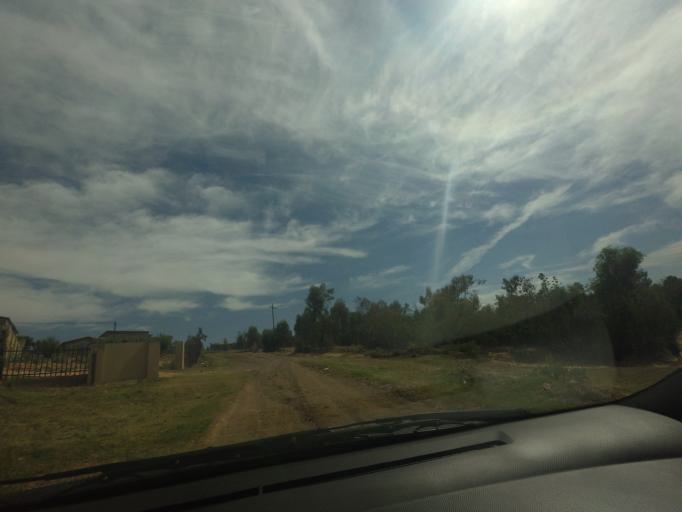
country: LS
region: Berea
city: Teyateyaneng
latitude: -29.1503
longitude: 27.7562
